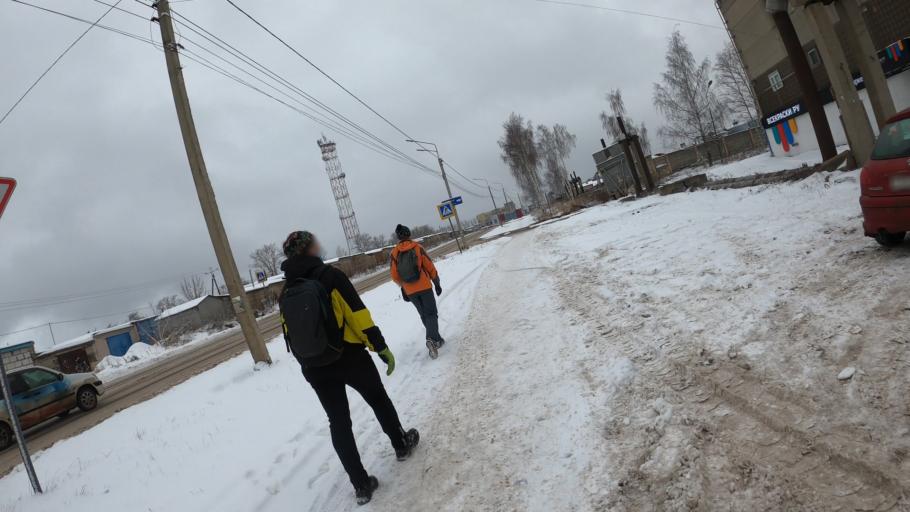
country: RU
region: Jaroslavl
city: Pereslavl'-Zalesskiy
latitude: 56.7441
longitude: 38.8926
